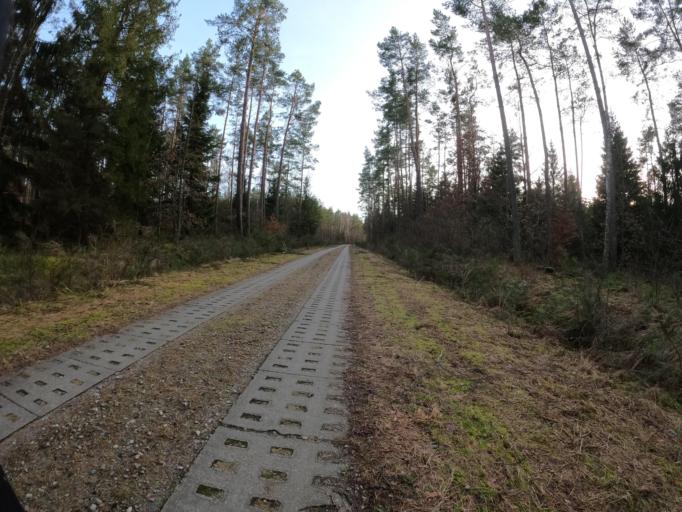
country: PL
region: West Pomeranian Voivodeship
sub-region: Powiat koszalinski
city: Polanow
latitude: 54.1299
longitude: 16.6638
